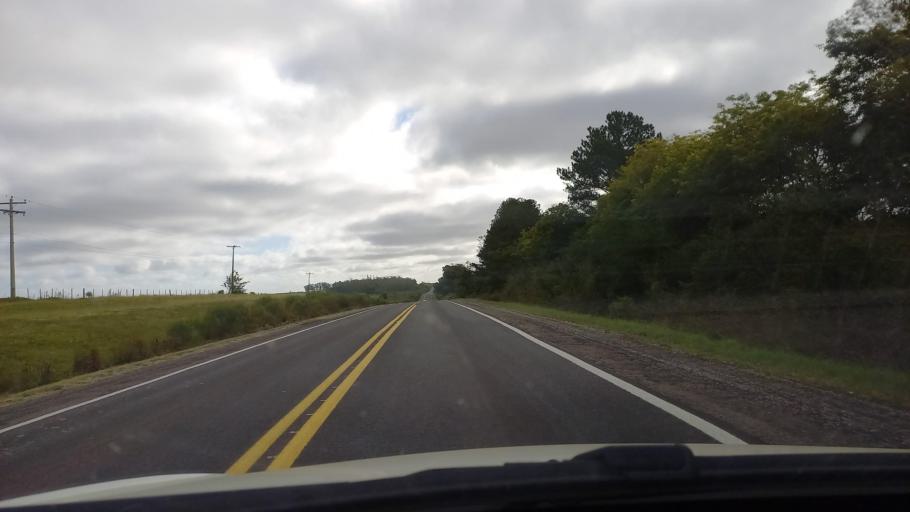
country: BR
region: Rio Grande do Sul
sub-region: Dom Pedrito
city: Dom Pedrito
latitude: -30.9168
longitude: -54.7942
